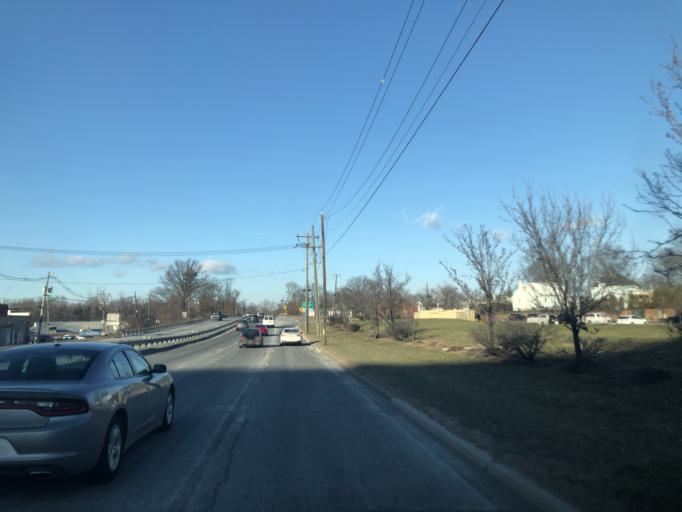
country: US
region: New Jersey
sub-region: Middlesex County
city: Woodbridge
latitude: 40.5480
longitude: -74.2909
